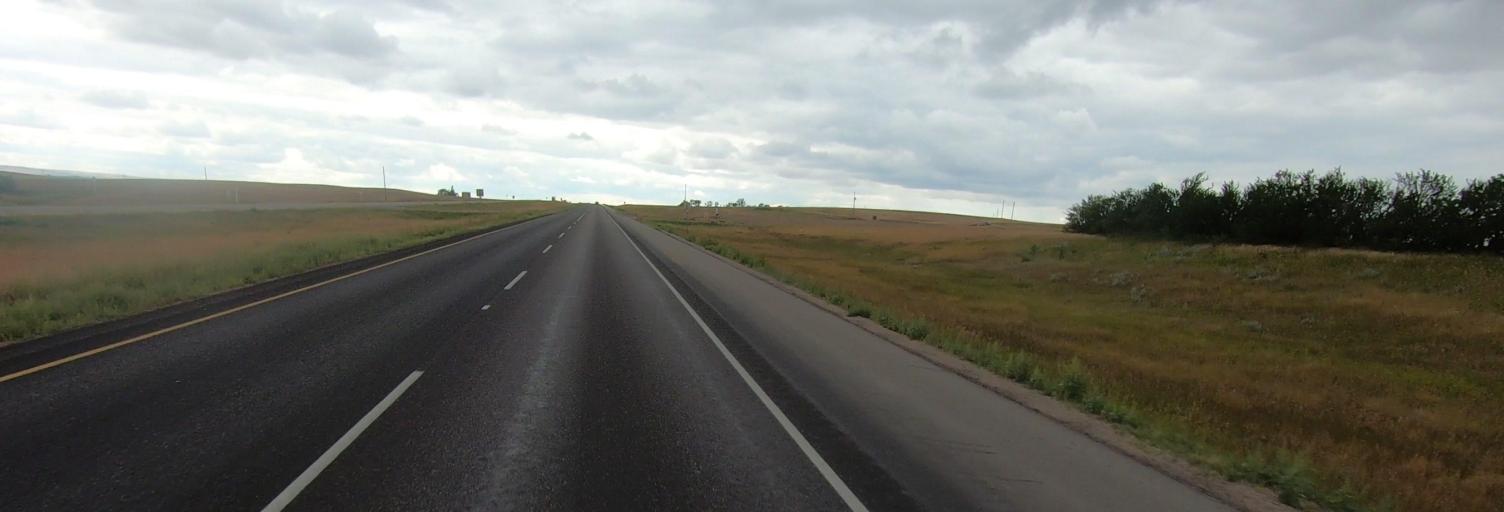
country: CA
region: Saskatchewan
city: Shaunavon
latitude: 50.0995
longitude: -108.4933
